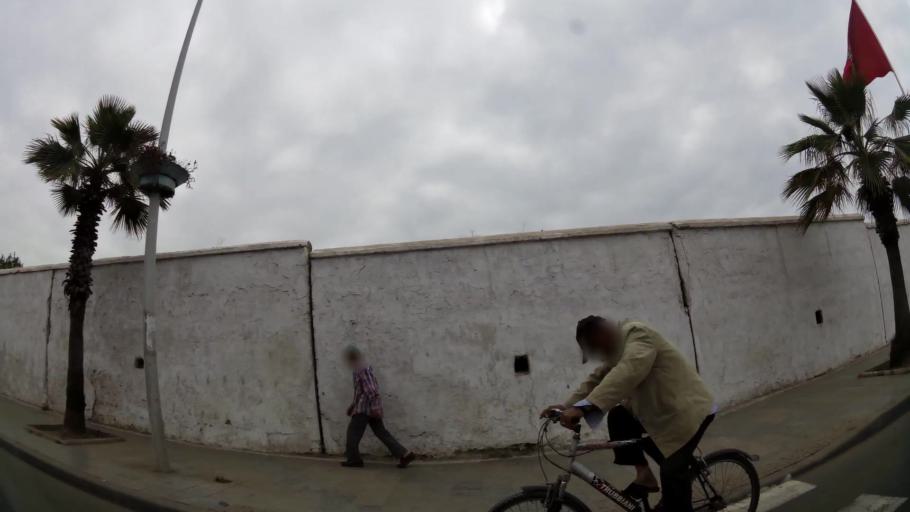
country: MA
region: Rabat-Sale-Zemmour-Zaer
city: Sale
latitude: 34.0352
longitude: -6.8121
